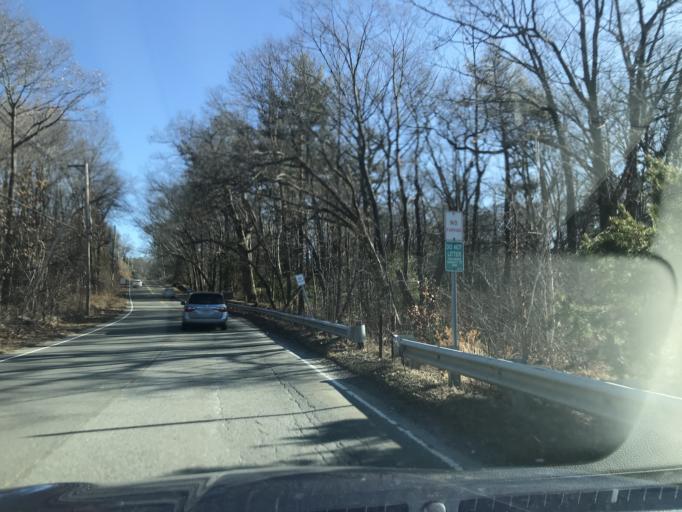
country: US
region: Massachusetts
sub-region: Essex County
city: North Andover
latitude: 42.7138
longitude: -71.0990
